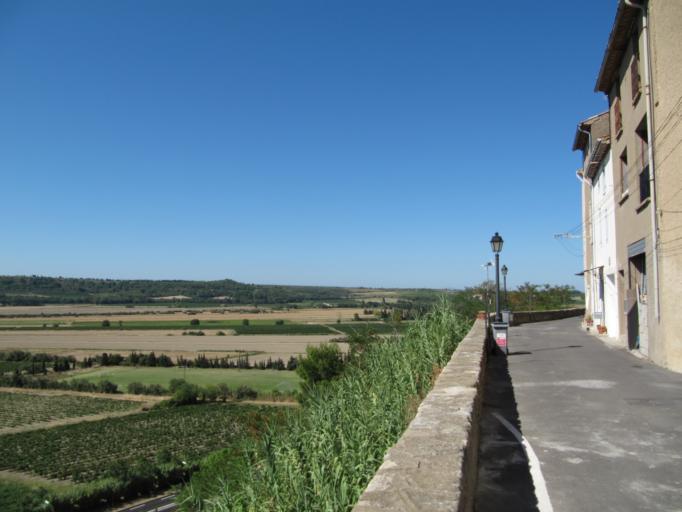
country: FR
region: Languedoc-Roussillon
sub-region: Departement de l'Herault
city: Montady
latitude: 43.3293
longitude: 3.1193
